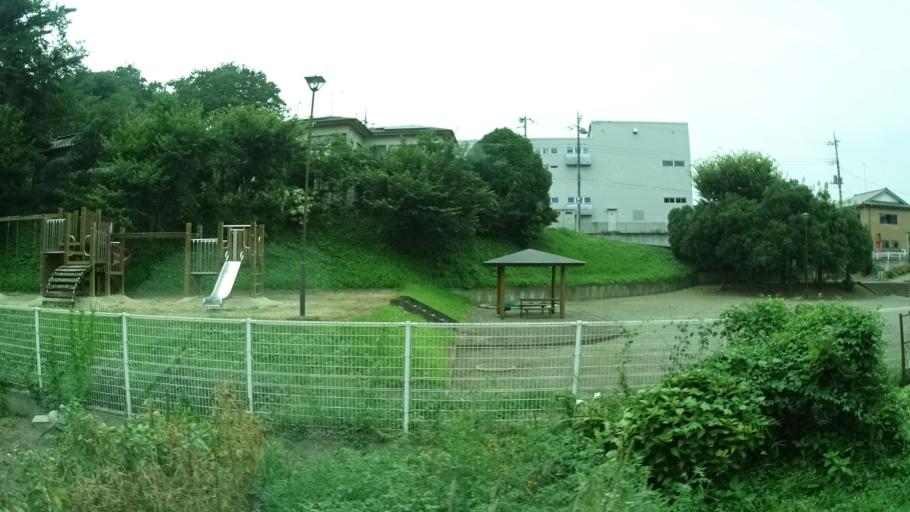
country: JP
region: Tochigi
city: Mooka
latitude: 36.3751
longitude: 139.9717
